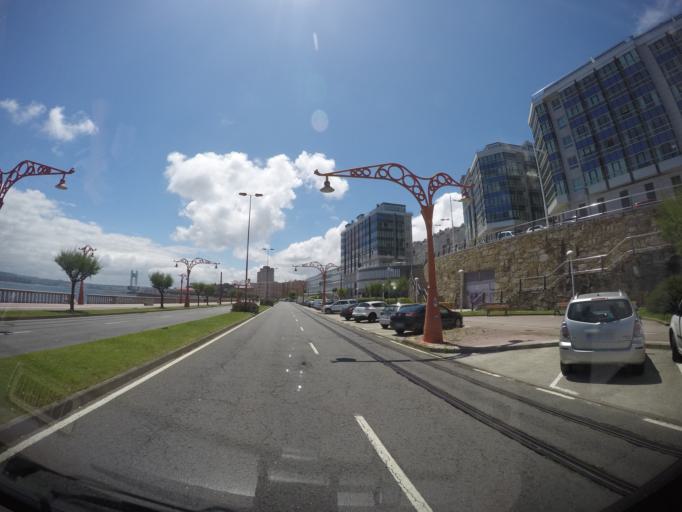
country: ES
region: Galicia
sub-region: Provincia da Coruna
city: A Coruna
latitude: 43.3729
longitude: -8.3905
